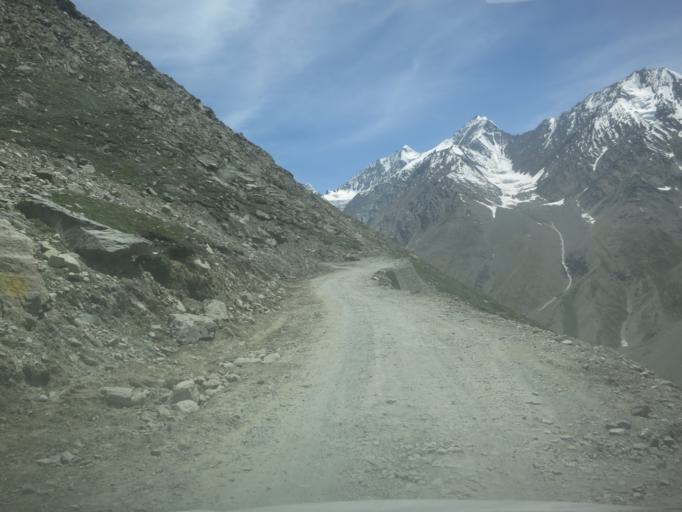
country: IN
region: Himachal Pradesh
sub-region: Kulu
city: Manali
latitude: 32.3874
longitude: 77.6266
